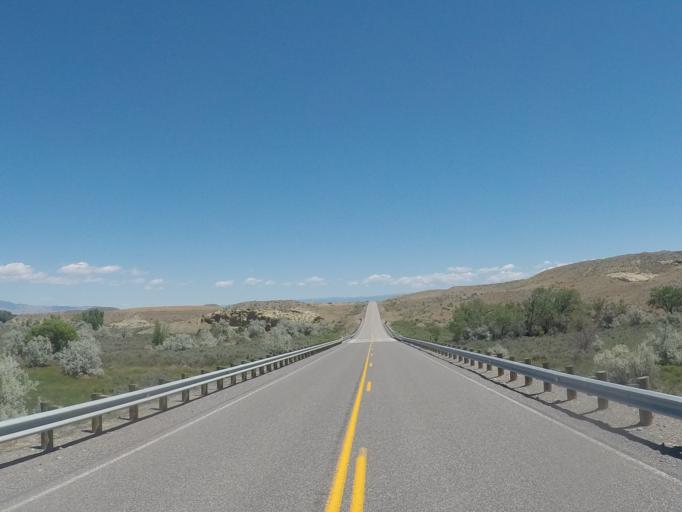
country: US
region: Wyoming
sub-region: Big Horn County
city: Lovell
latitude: 44.7681
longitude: -108.5176
